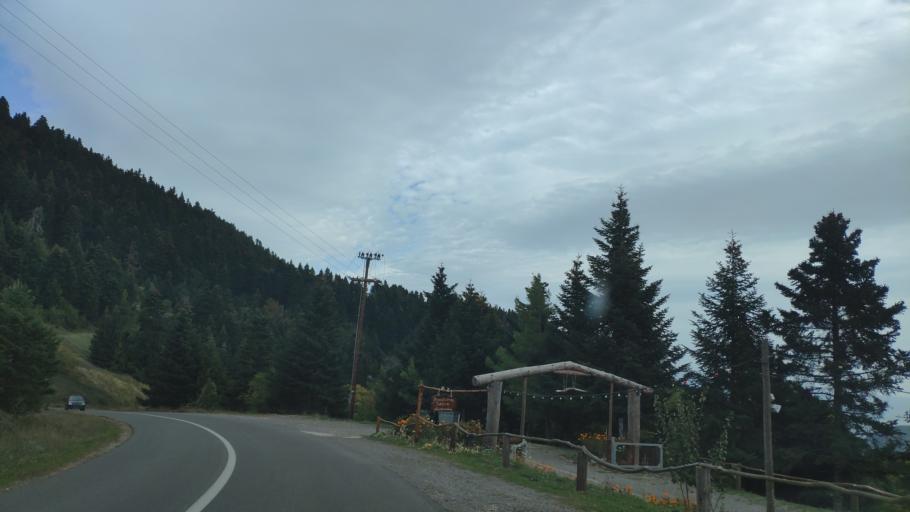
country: GR
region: Central Greece
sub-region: Nomos Fthiotidos
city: Stavros
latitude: 38.7289
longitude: 22.3390
